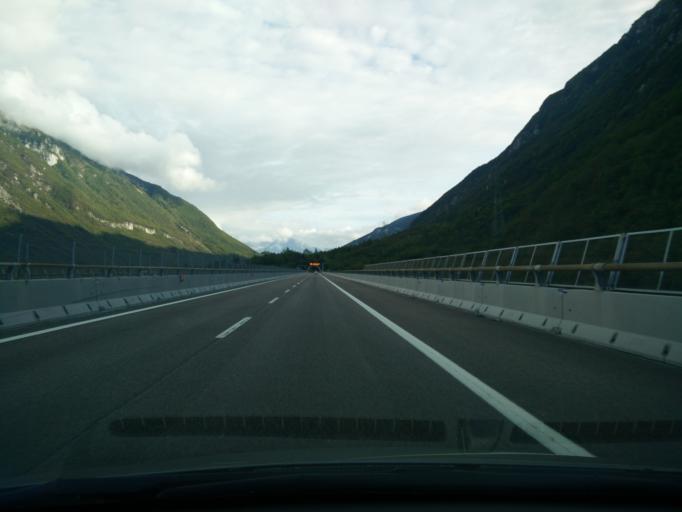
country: IT
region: Veneto
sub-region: Provincia di Treviso
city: Fregona
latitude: 46.0362
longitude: 12.3090
